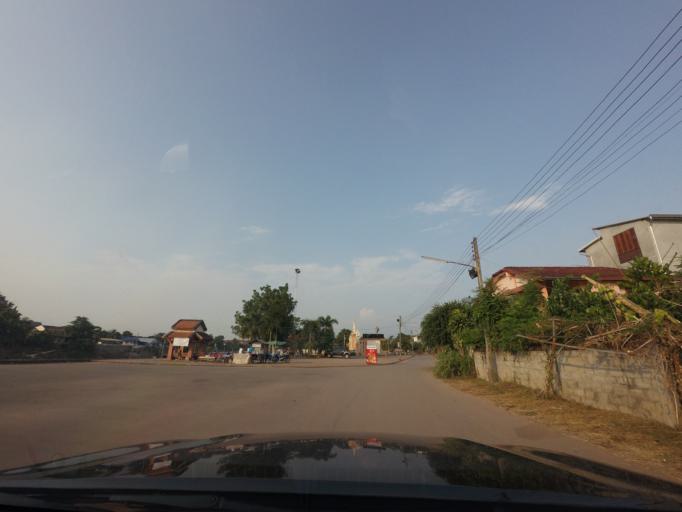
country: TH
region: Nan
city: Nan
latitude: 18.7773
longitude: 100.7832
